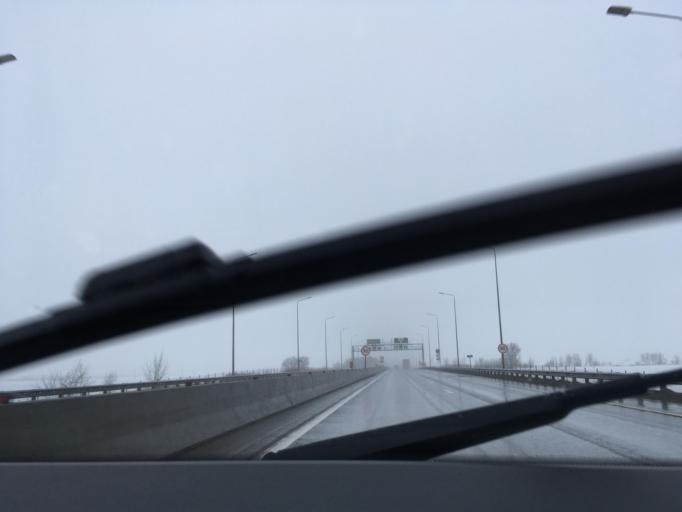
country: RU
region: Rostov
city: Samarskoye
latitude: 46.9061
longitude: 39.7056
